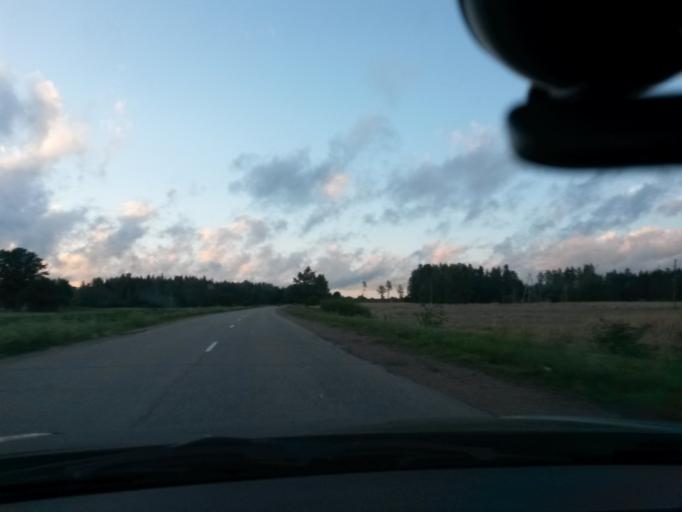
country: LV
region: Jekabpils Rajons
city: Jekabpils
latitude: 56.7015
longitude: 25.9811
